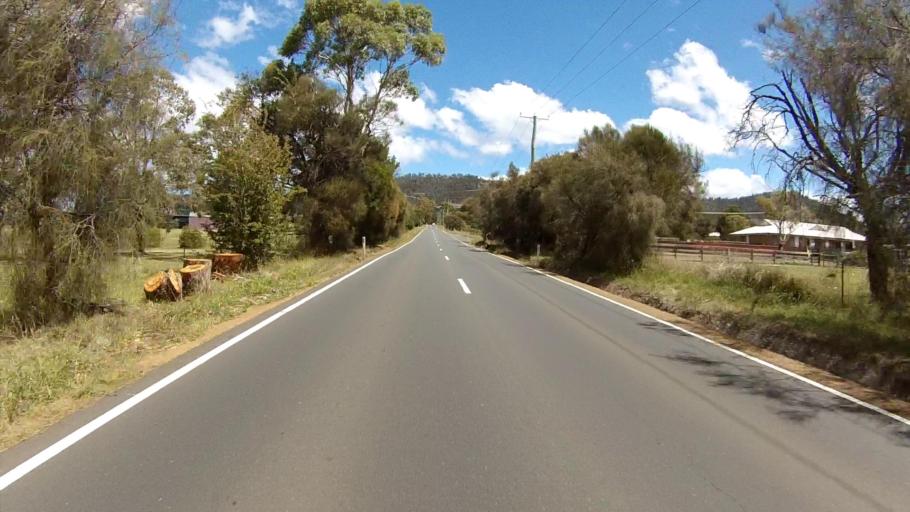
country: AU
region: Tasmania
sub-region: Clarence
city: Seven Mile Beach
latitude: -42.8494
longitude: 147.4767
